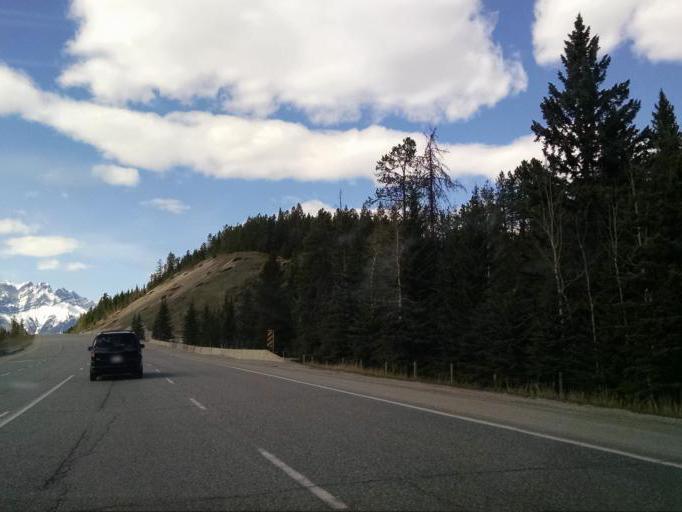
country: CA
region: Alberta
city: Canmore
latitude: 51.1372
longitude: -115.4089
